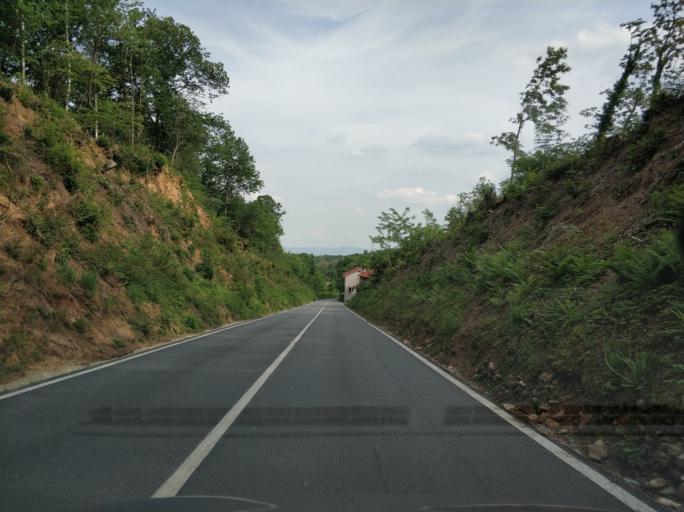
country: IT
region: Piedmont
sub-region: Provincia di Torino
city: Corio
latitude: 45.3035
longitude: 7.5398
